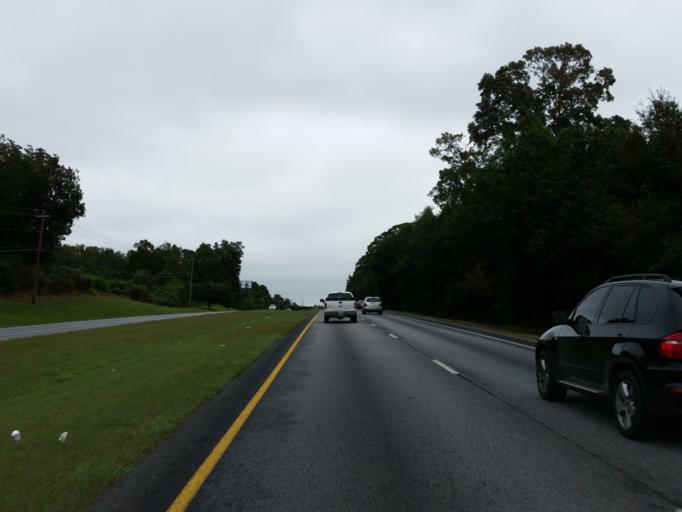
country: US
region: Georgia
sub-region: Clayton County
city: Irondale
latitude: 33.4997
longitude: -84.3474
